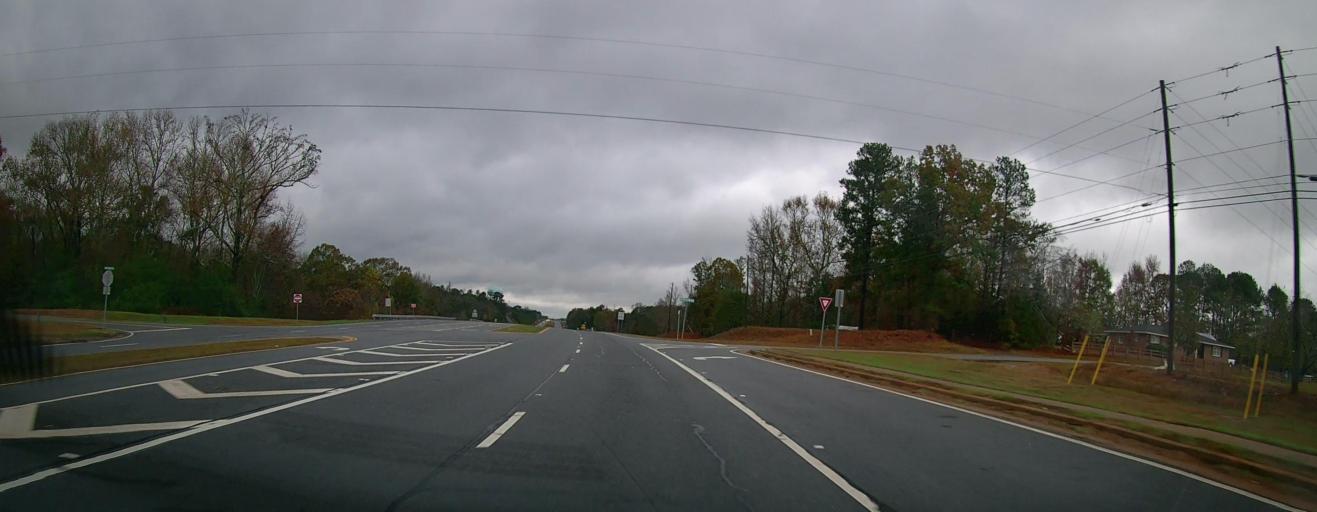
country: US
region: Georgia
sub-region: Jackson County
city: Nicholson
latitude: 34.1326
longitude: -83.4285
